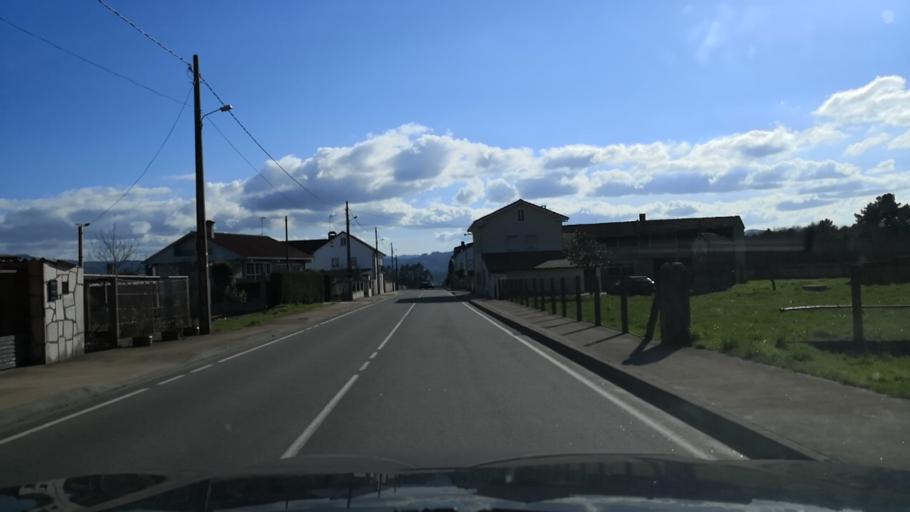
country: ES
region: Galicia
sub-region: Provincia da Coruna
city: Ribeira
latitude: 42.7120
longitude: -8.4464
